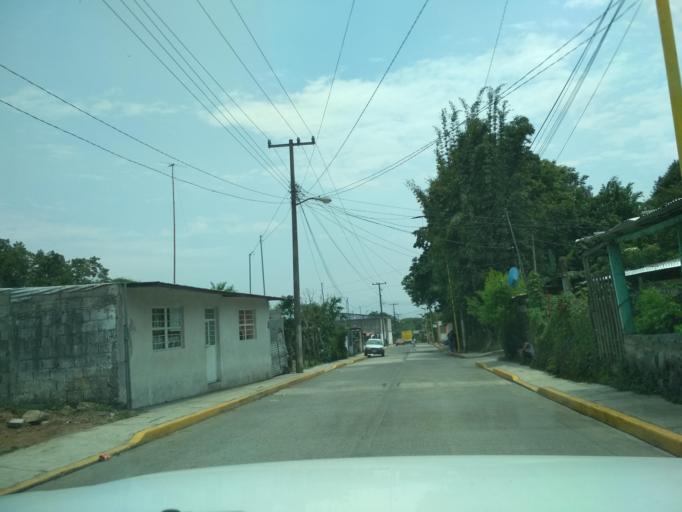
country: MX
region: Veracruz
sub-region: Mariano Escobedo
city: Mariano Escobedo
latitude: 18.9099
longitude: -97.1287
